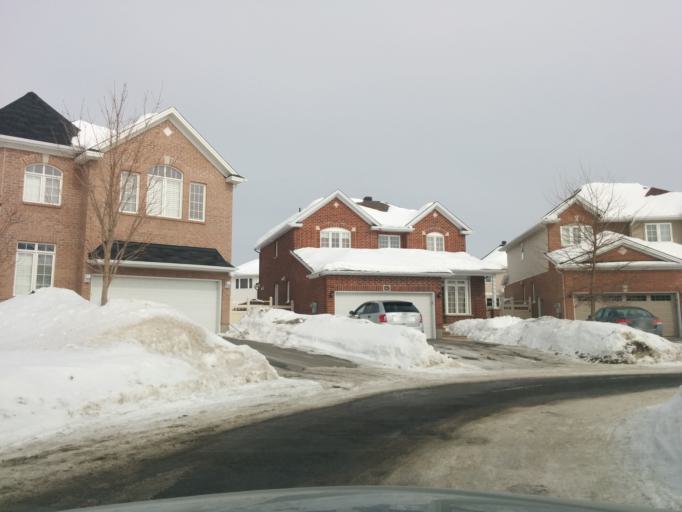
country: CA
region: Ontario
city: Ottawa
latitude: 45.3687
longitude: -75.7414
